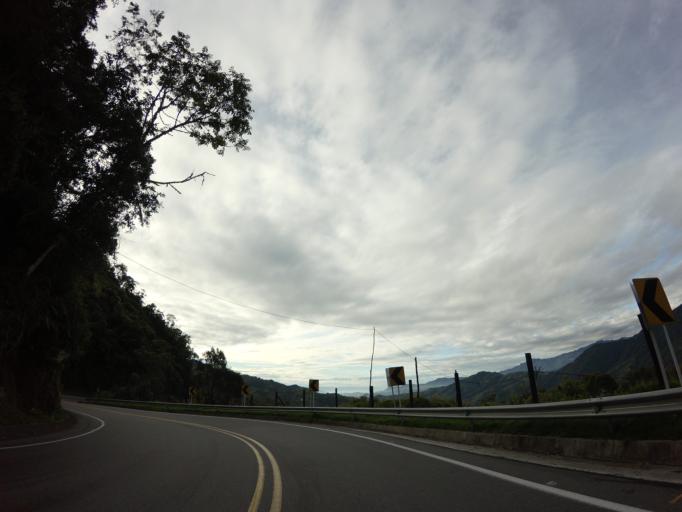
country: CO
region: Tolima
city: Herveo
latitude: 5.1054
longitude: -75.2547
